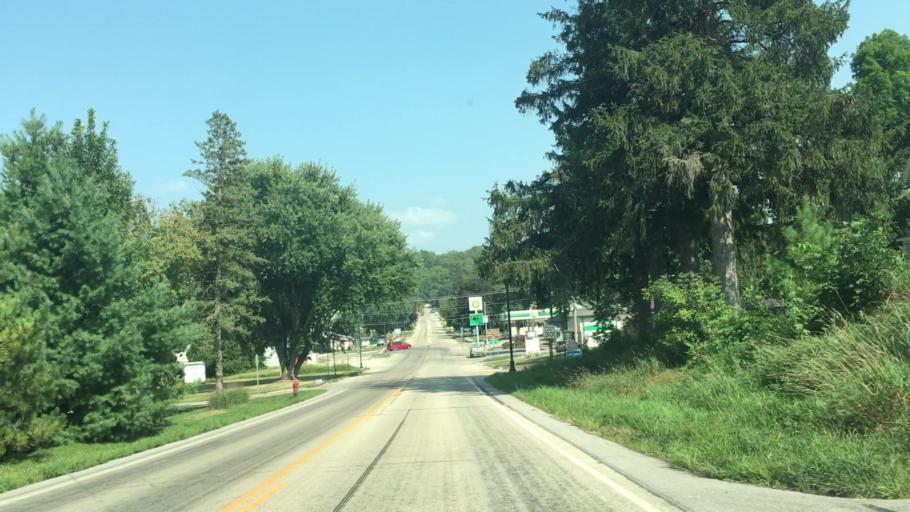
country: US
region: Minnesota
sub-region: Fillmore County
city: Preston
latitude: 43.7140
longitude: -91.9792
